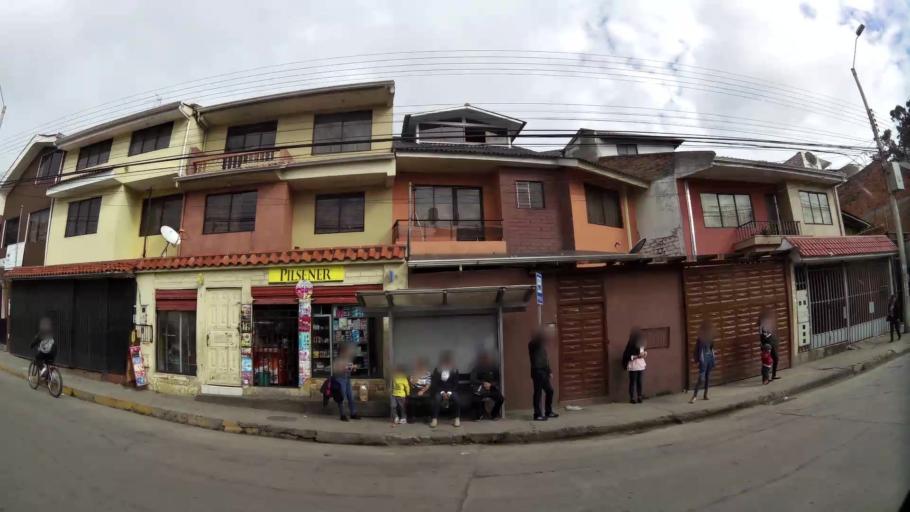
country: EC
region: Azuay
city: Cuenca
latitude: -2.8934
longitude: -78.9762
